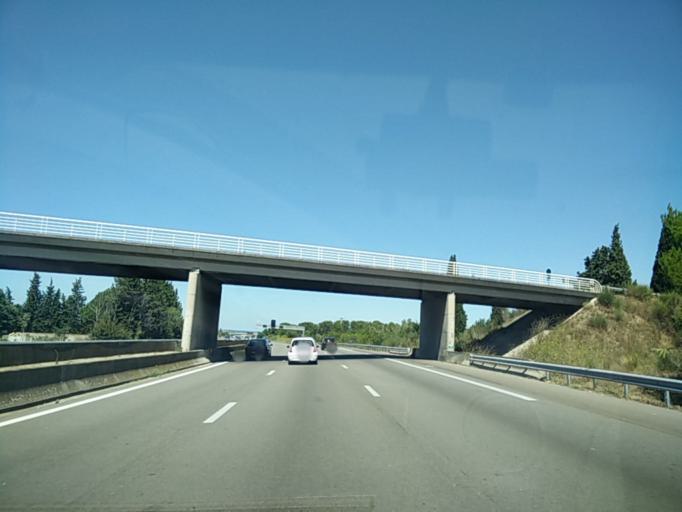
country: FR
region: Provence-Alpes-Cote d'Azur
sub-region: Departement du Vaucluse
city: Morieres-les-Avignon
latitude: 43.9476
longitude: 4.9107
